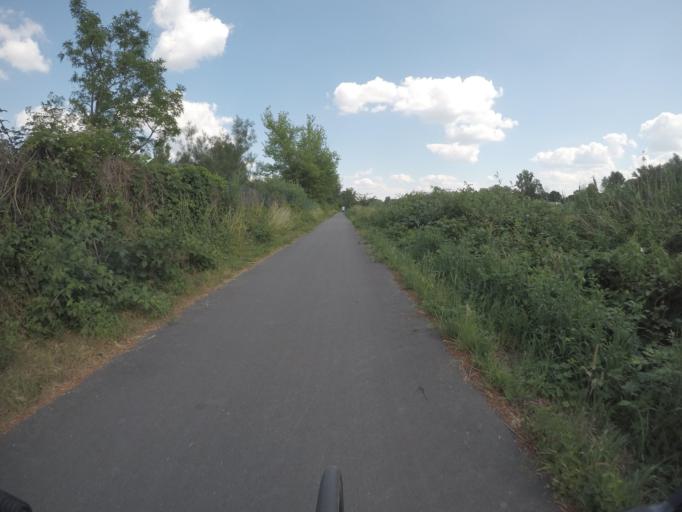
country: DE
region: Brandenburg
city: Roskow
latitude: 52.4533
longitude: 12.7778
